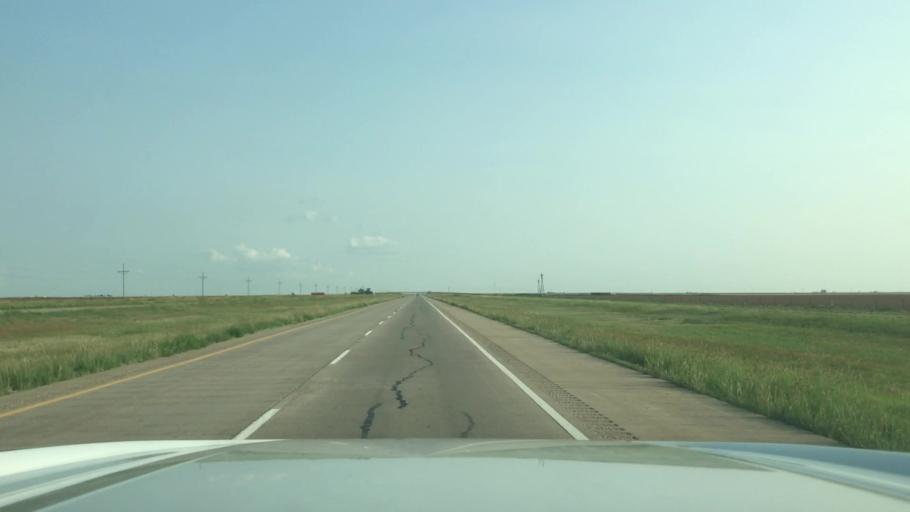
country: US
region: Texas
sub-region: Randall County
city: Canyon
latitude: 34.9089
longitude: -101.8487
